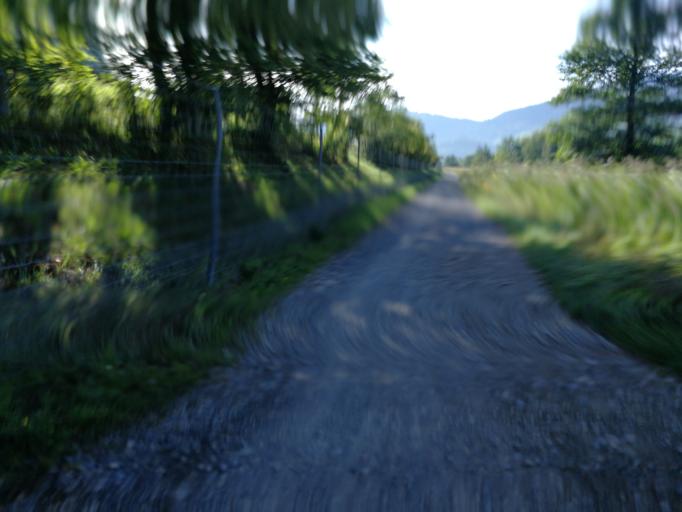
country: CH
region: Schwyz
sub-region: Bezirk Schwyz
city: Goldau
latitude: 47.0481
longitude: 8.5745
